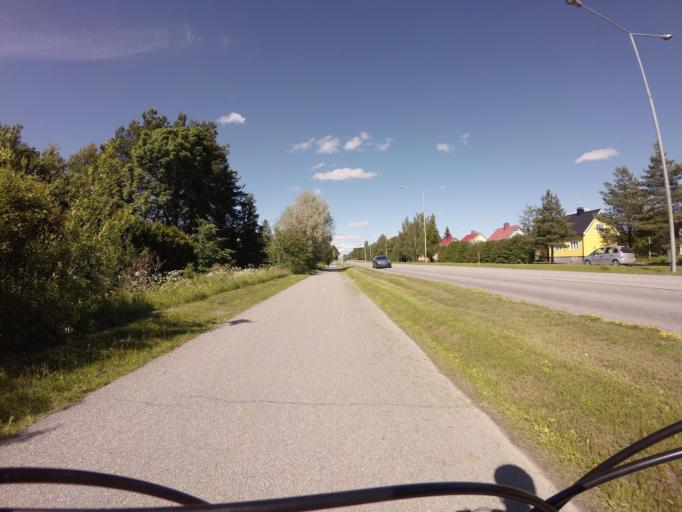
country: FI
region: Varsinais-Suomi
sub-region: Turku
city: Turku
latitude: 60.4790
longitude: 22.2693
